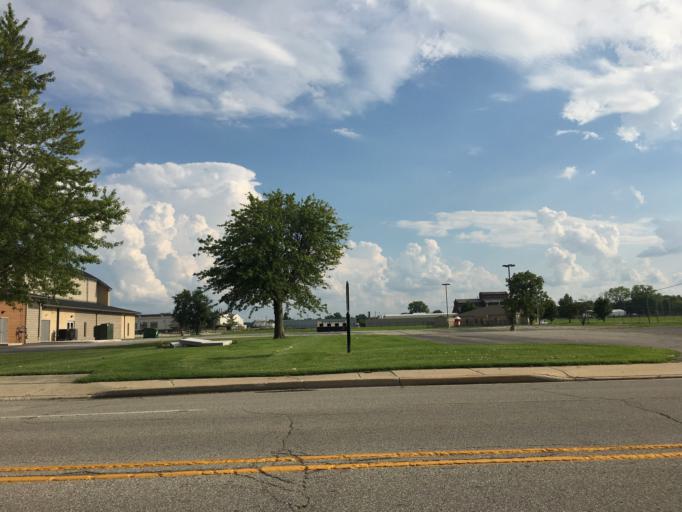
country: US
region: Indiana
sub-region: Howard County
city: Kokomo
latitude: 40.4662
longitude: -86.1201
